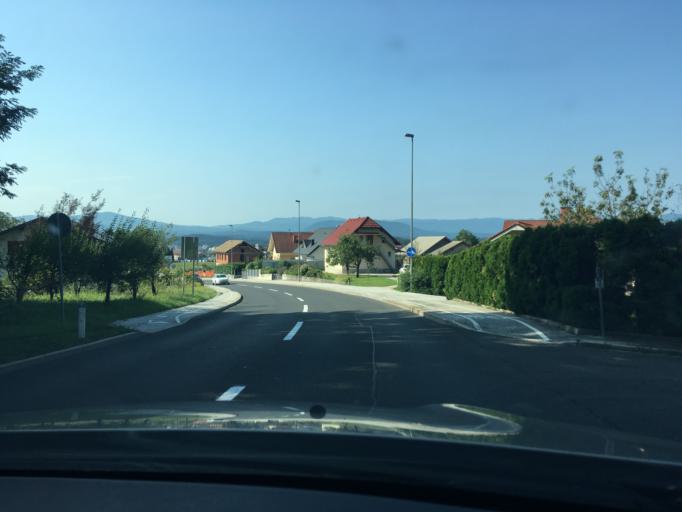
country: SI
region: Novo Mesto
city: Novo Mesto
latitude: 45.8362
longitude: 15.1557
